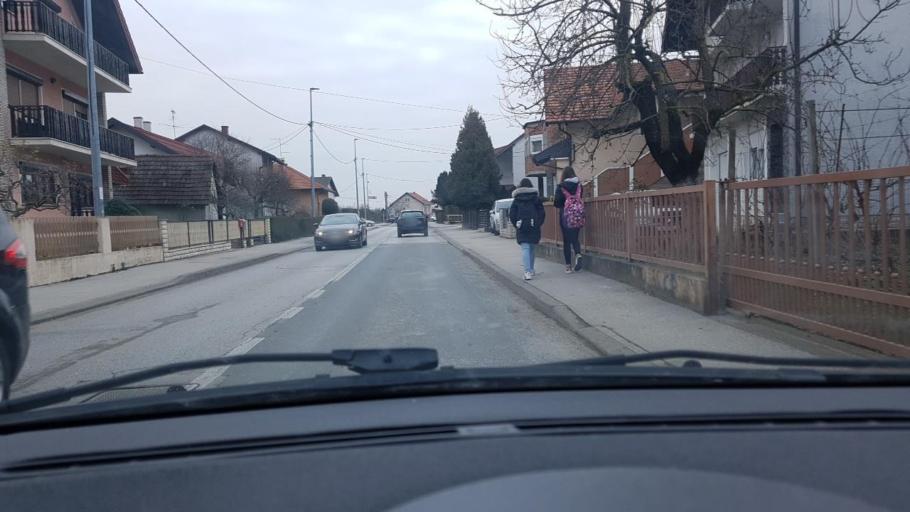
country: HR
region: Zagrebacka
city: Zapresic
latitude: 45.8623
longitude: 15.7968
